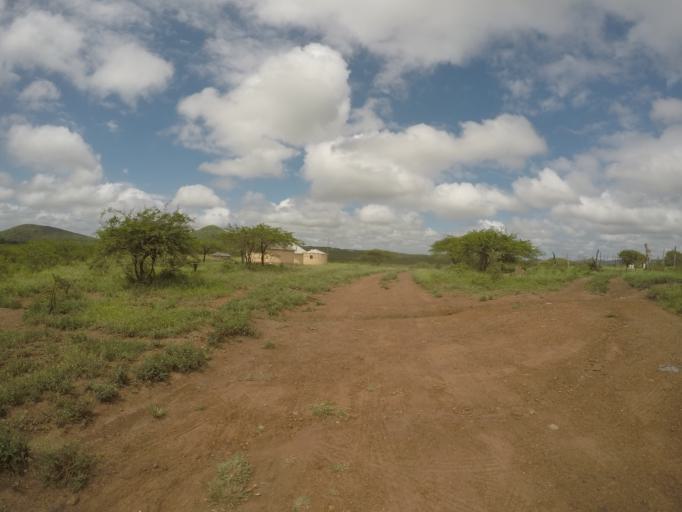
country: ZA
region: KwaZulu-Natal
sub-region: uThungulu District Municipality
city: Empangeni
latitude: -28.5835
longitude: 31.8531
